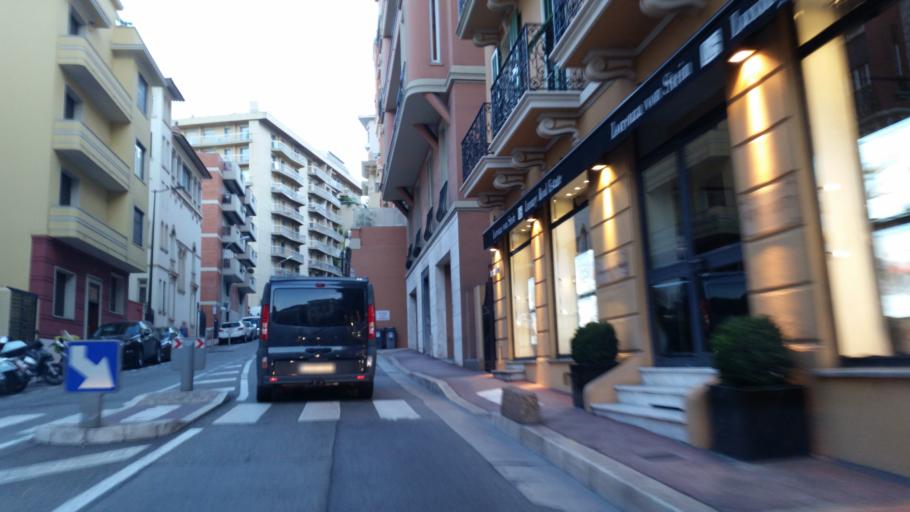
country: MC
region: Commune de Monaco
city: Moneghetti
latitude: 43.7366
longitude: 7.4163
